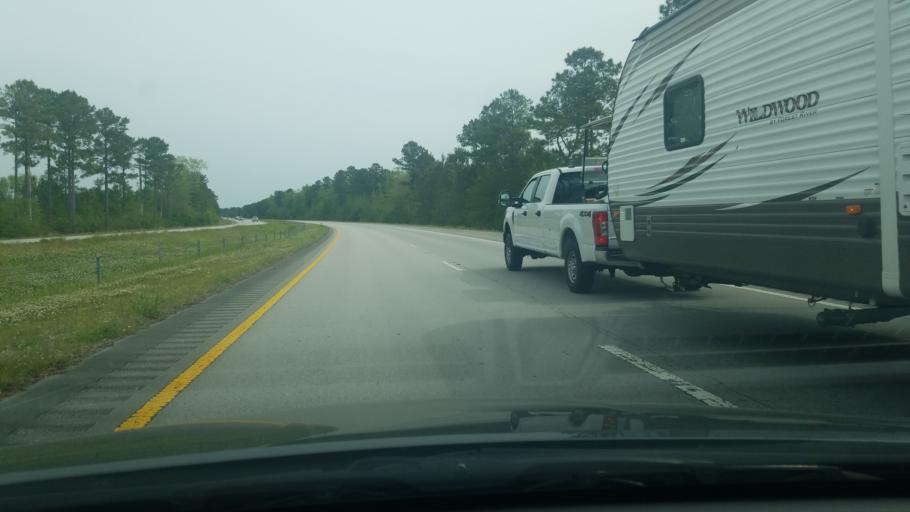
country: US
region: North Carolina
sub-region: Craven County
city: River Bend
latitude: 35.1079
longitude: -77.1633
